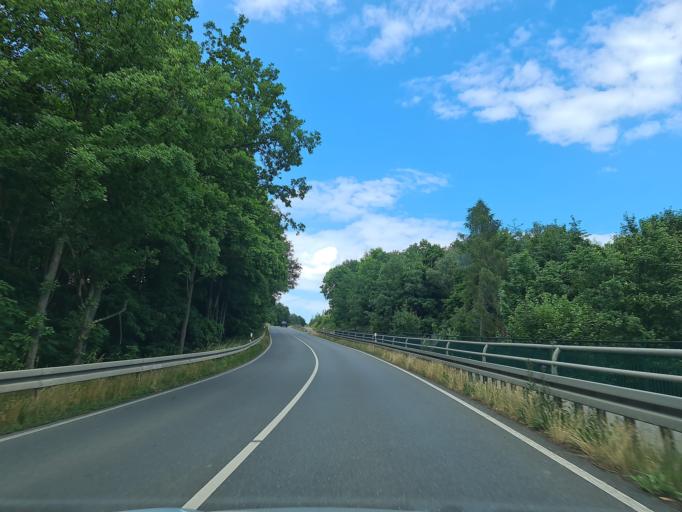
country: DE
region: Saxony
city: Pohl
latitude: 50.5336
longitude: 12.1806
